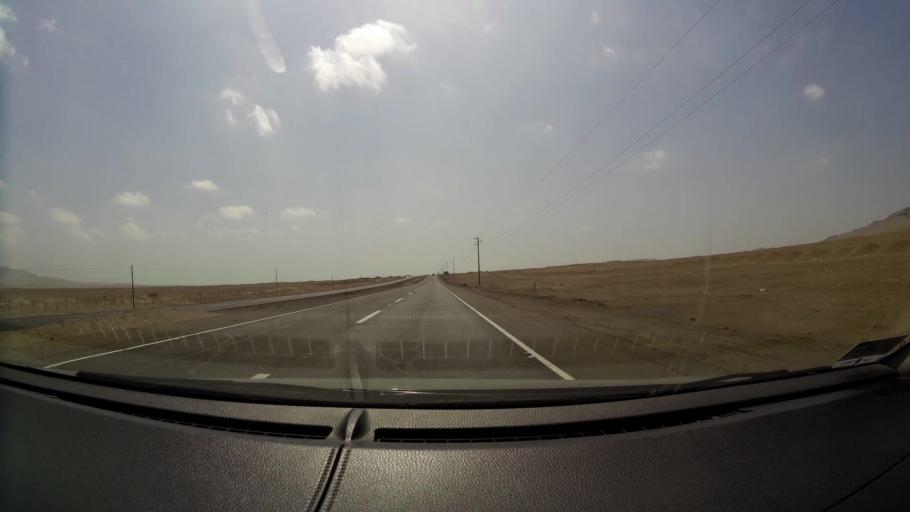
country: PE
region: Lima
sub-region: Huaura
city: Huacho
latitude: -11.2341
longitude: -77.5405
